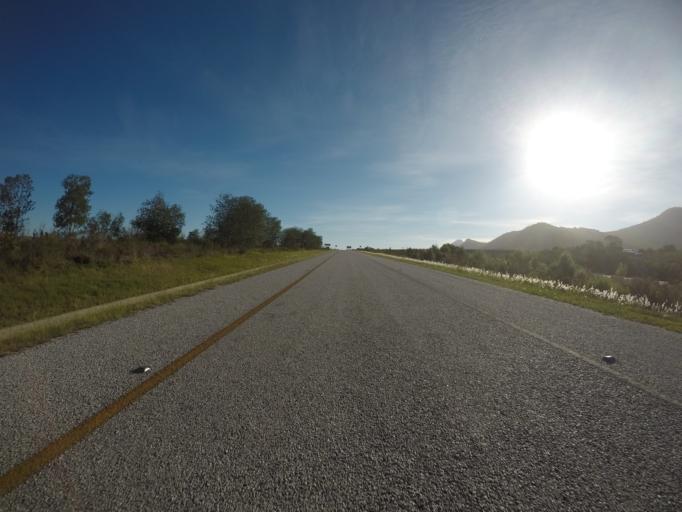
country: ZA
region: Eastern Cape
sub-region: Cacadu District Municipality
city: Kareedouw
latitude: -33.9995
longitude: 24.2378
